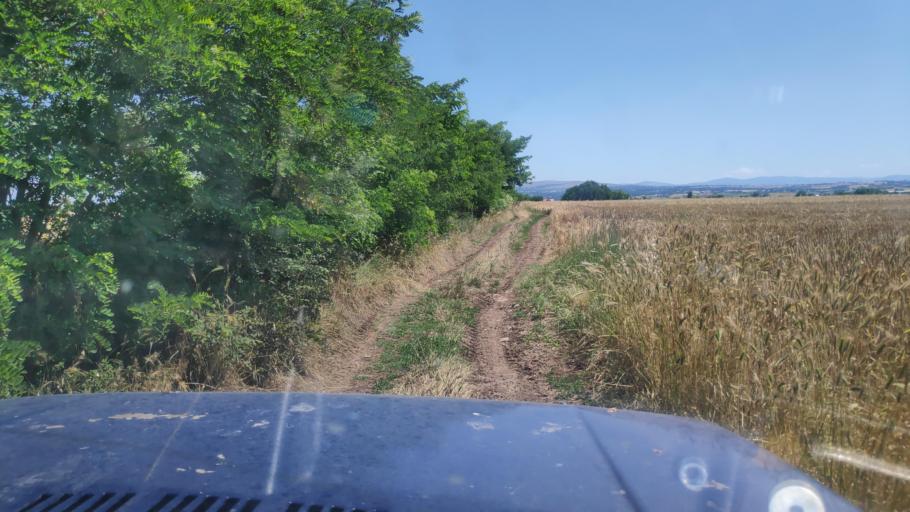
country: MK
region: Kumanovo
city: Bedinje
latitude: 42.1698
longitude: 21.6878
